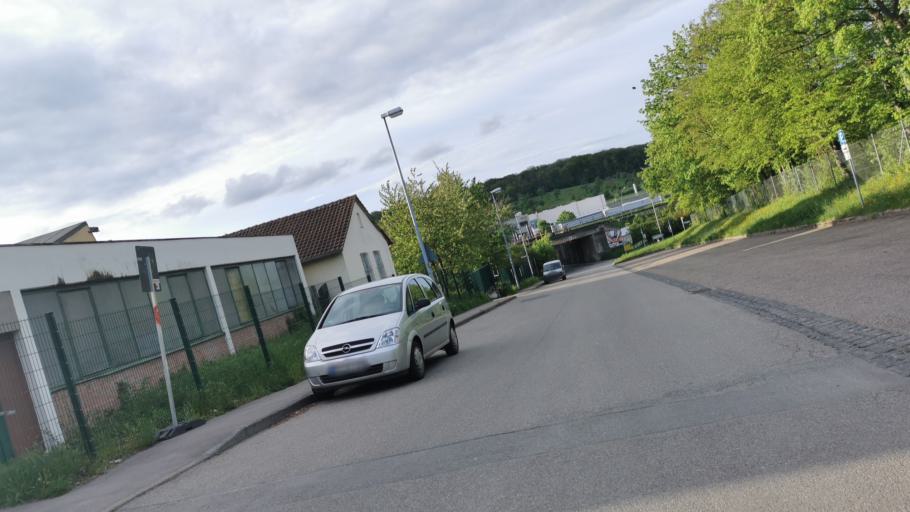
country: DE
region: Baden-Wuerttemberg
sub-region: Regierungsbezirk Stuttgart
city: Korntal
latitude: 48.8292
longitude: 9.1344
